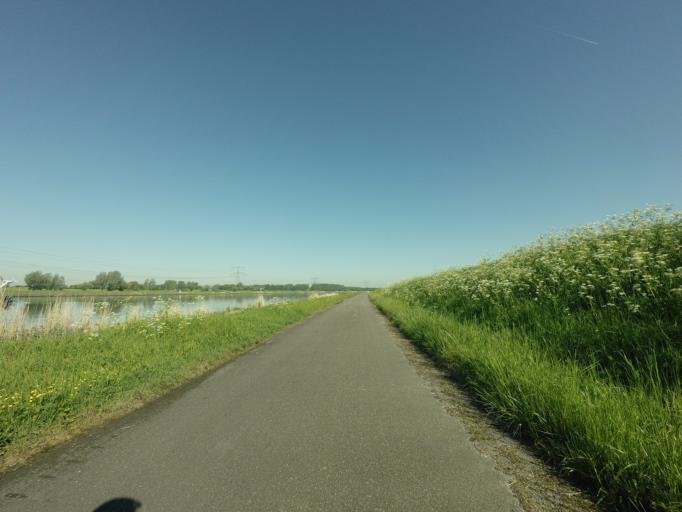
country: NL
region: North Brabant
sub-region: Gemeente Woensdrecht
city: Woensdrecht
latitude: 51.3865
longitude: 4.2487
